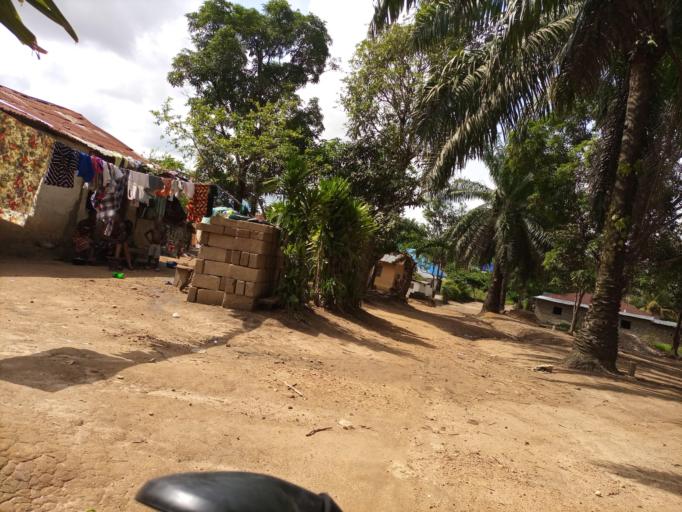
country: SL
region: Southern Province
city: Bo
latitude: 7.9598
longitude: -11.7611
